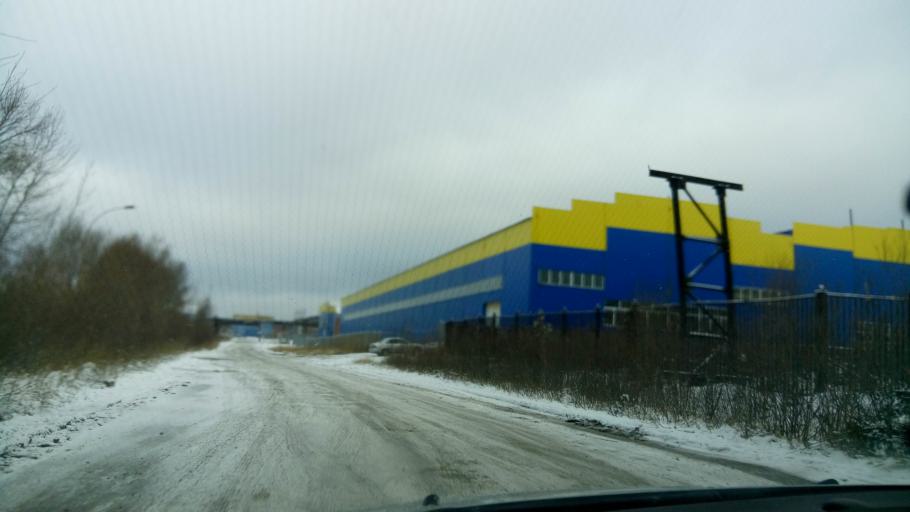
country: RU
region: Sverdlovsk
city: Polevskoy
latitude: 56.4689
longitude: 60.1774
